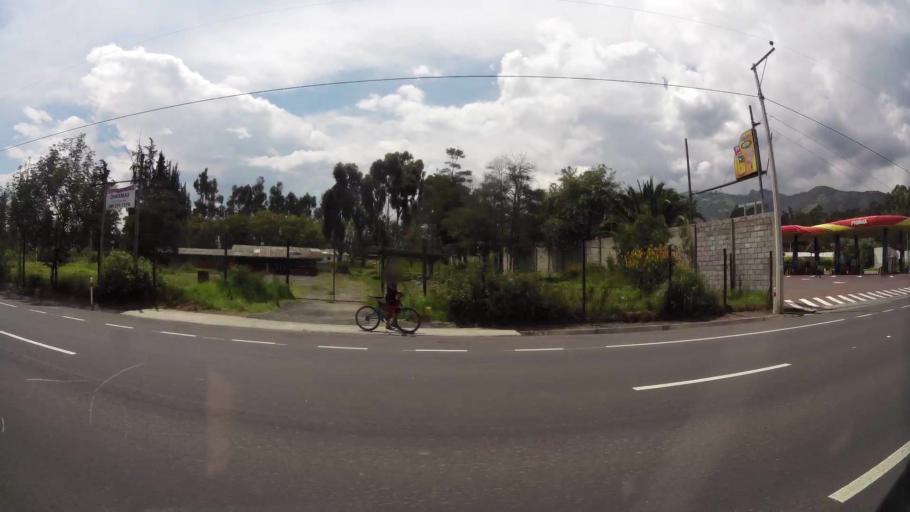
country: EC
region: Pichincha
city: Sangolqui
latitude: -0.2044
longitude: -78.3336
